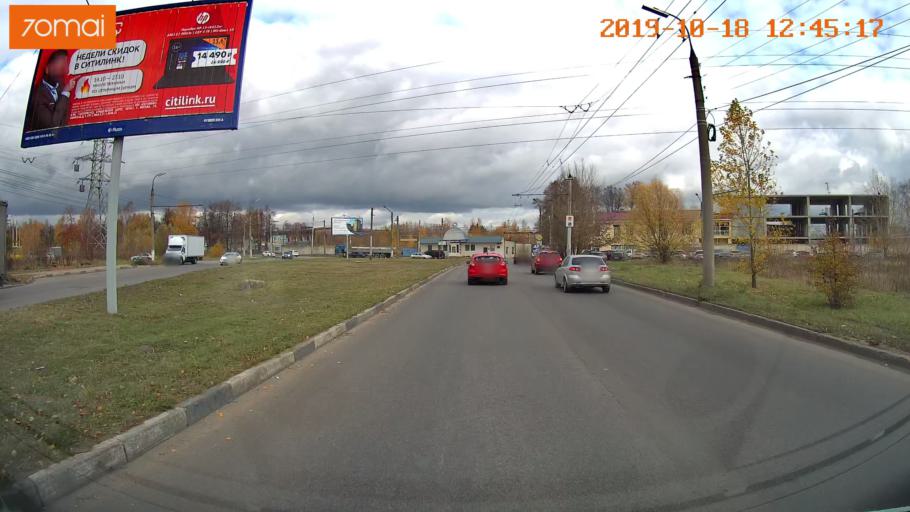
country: RU
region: Rjazan
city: Ryazan'
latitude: 54.6515
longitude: 39.6655
